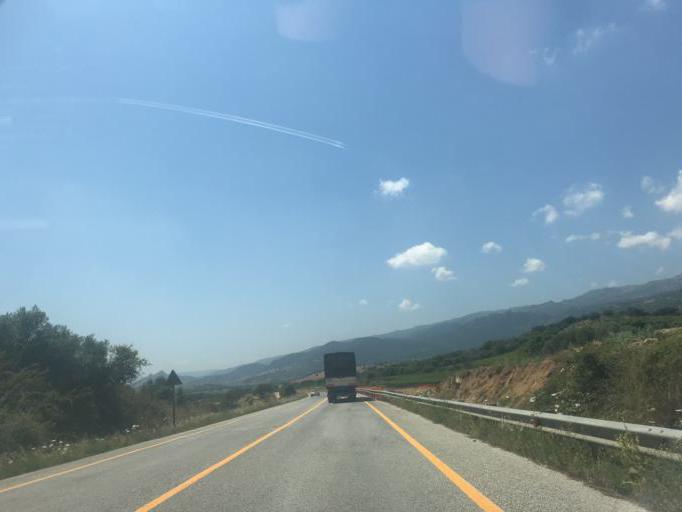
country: IT
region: Sardinia
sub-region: Provincia di Olbia-Tempio
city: Berchidda
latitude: 40.7808
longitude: 9.2234
